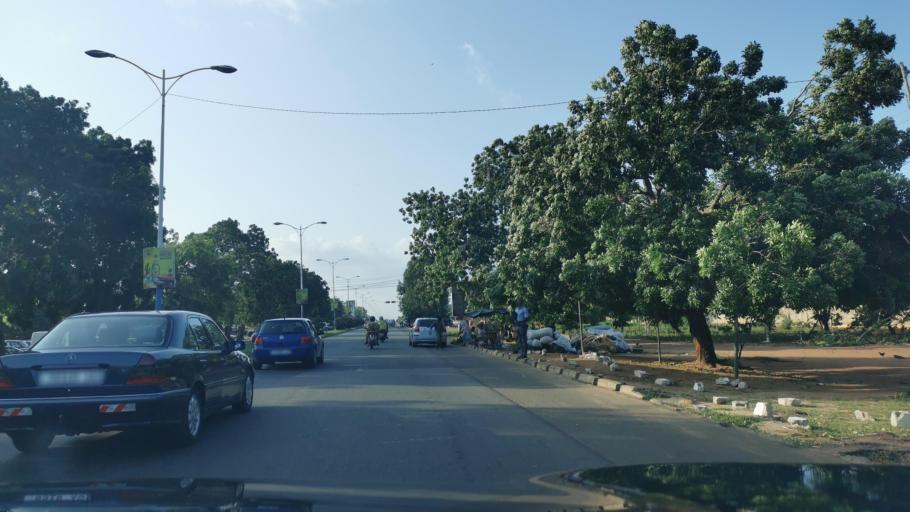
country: TG
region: Maritime
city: Lome
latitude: 6.2024
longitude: 1.2086
